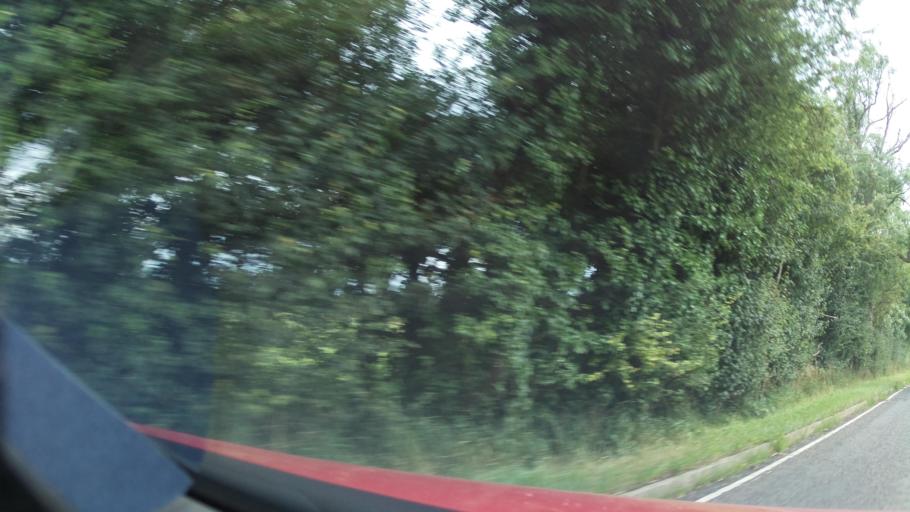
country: GB
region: England
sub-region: Warwickshire
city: Long Itchington
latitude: 52.2902
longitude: -1.3498
